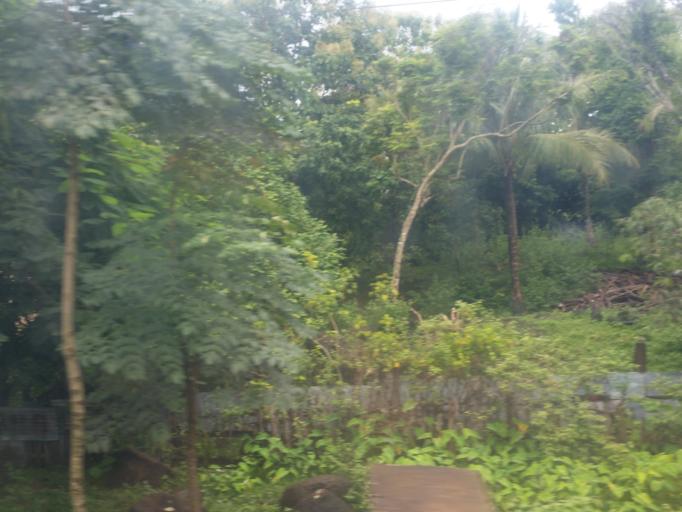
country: LA
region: Xekong
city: Thateng
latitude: 15.5403
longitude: 106.2648
